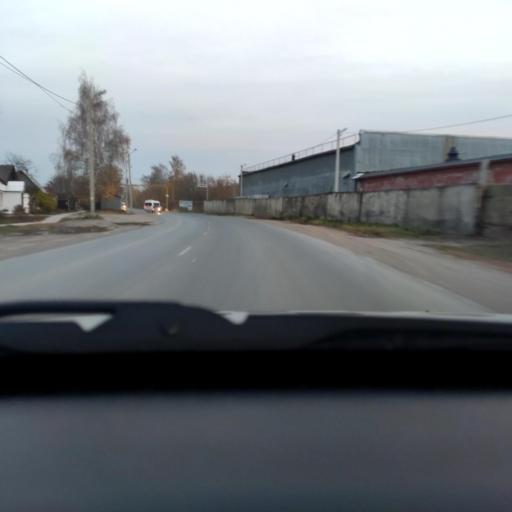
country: RU
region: Perm
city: Kondratovo
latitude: 57.9501
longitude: 56.1389
